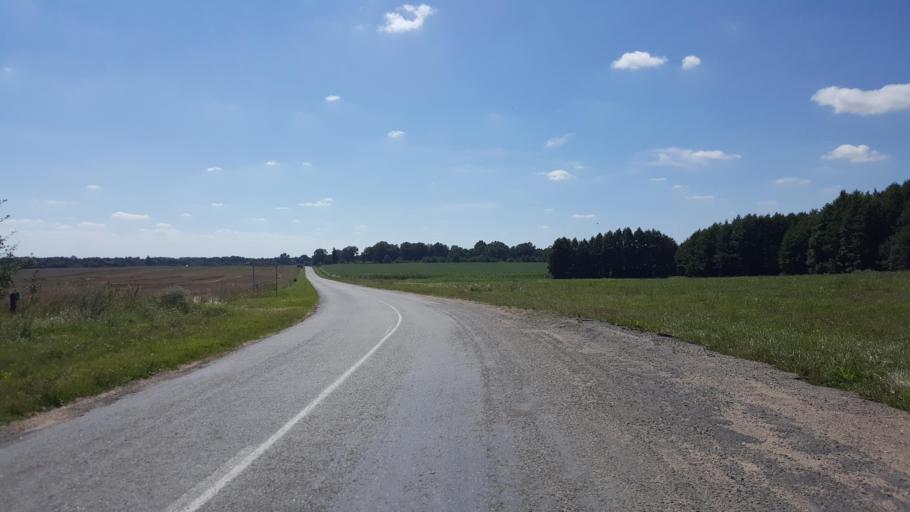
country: BY
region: Brest
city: Charnawchytsy
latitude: 52.3386
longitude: 23.6048
